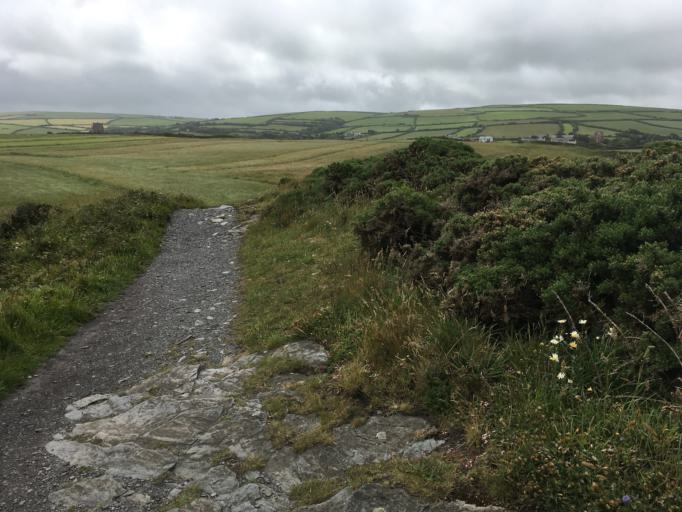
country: GB
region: England
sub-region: Cornwall
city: Tintagel
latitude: 50.6890
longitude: -4.7030
